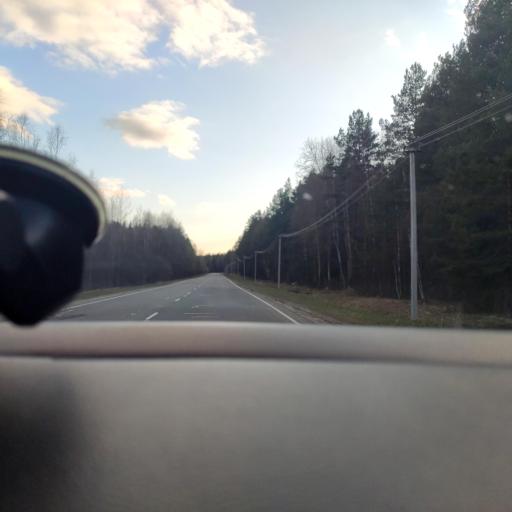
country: RU
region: Moskovskaya
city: Shaturtorf
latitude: 55.4529
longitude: 39.4475
